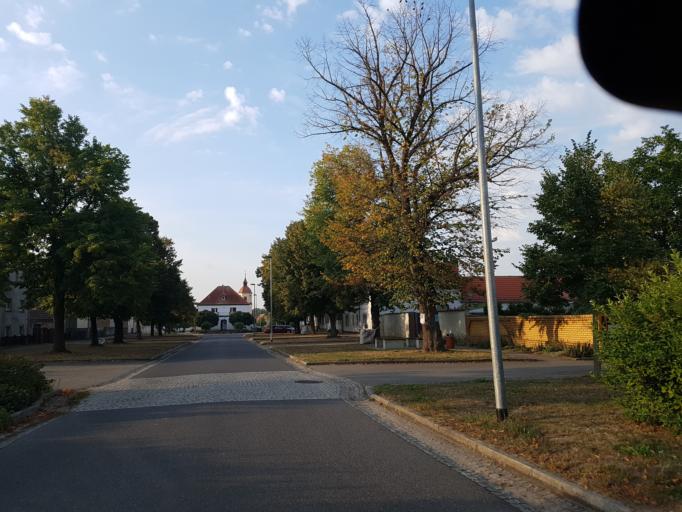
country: DE
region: Brandenburg
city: Hohenleipisch
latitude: 51.4687
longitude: 13.5661
